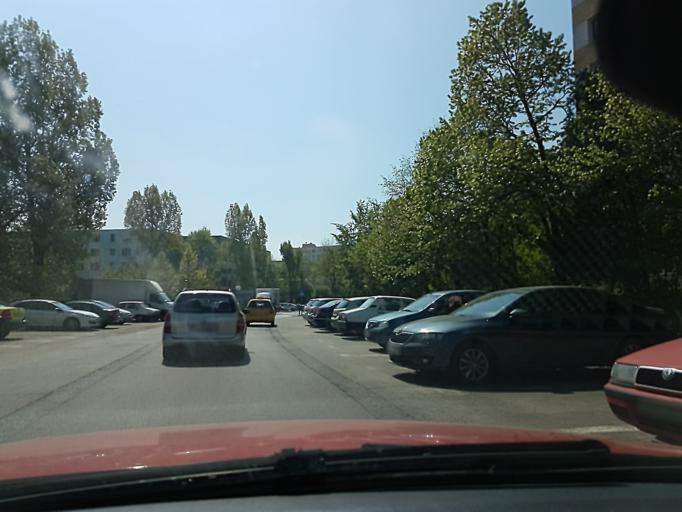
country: RO
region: Ilfov
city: Dobroesti
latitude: 44.4181
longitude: 26.1799
